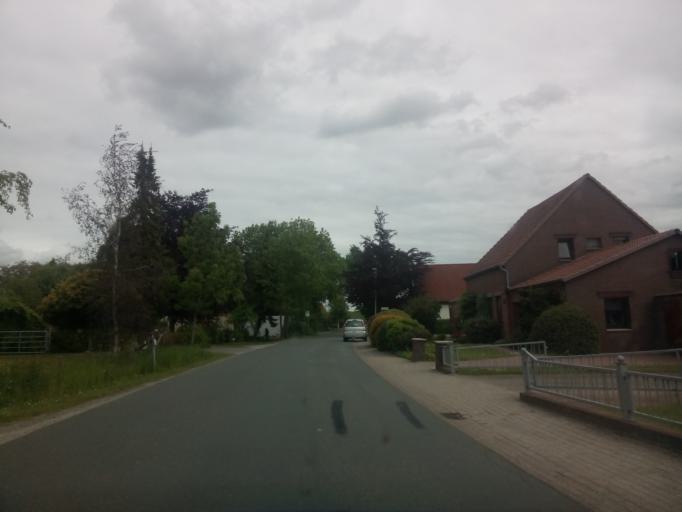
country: DE
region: Lower Saxony
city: Lemwerder
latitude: 53.1746
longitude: 8.5683
